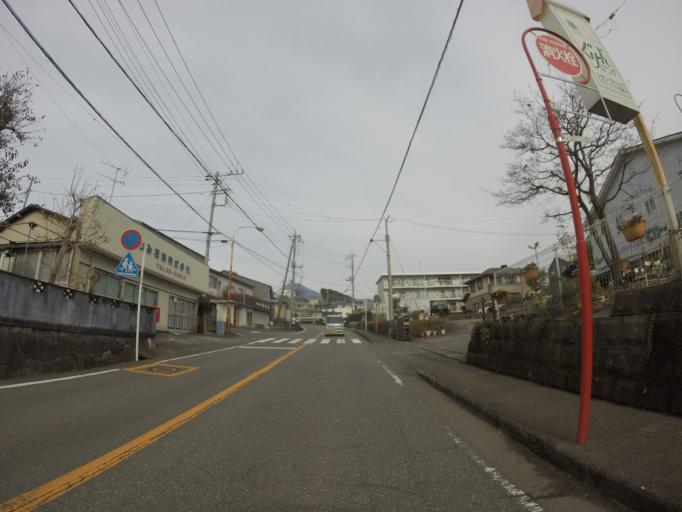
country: JP
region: Shizuoka
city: Fuji
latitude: 35.1890
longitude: 138.6835
